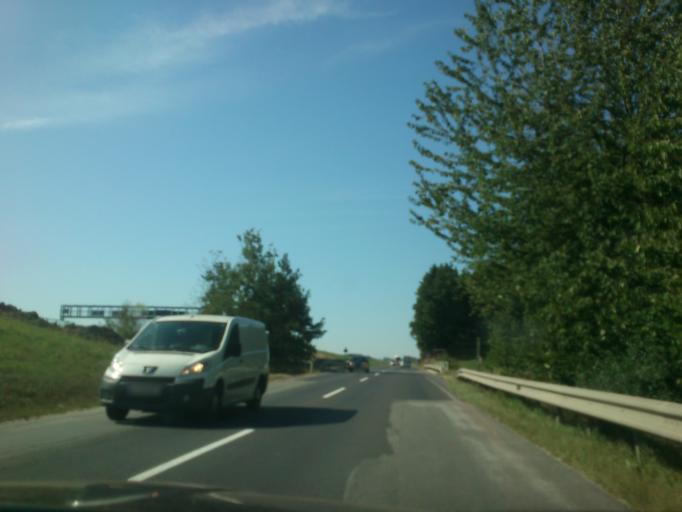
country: AT
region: Upper Austria
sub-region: Politischer Bezirk Freistadt
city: Freistadt
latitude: 48.4607
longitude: 14.5012
